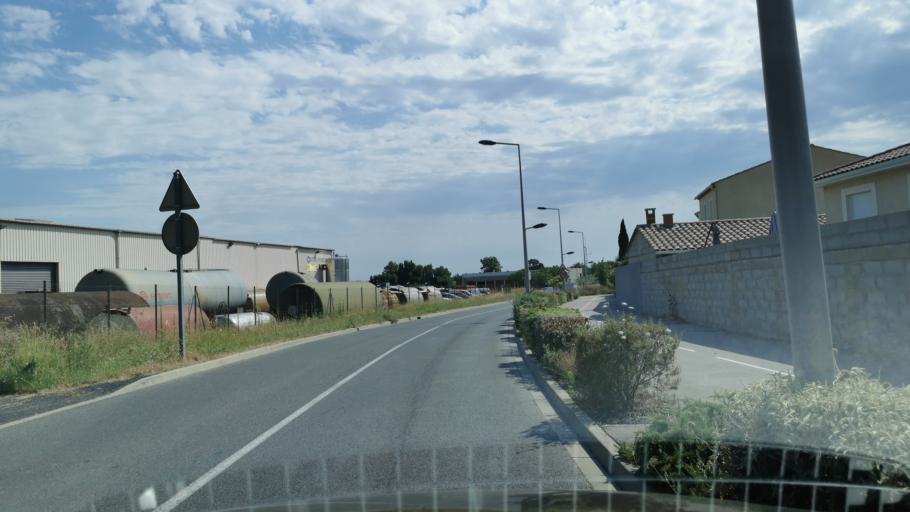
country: FR
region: Languedoc-Roussillon
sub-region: Departement de l'Herault
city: Cazouls-les-Beziers
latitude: 43.3846
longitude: 3.1042
